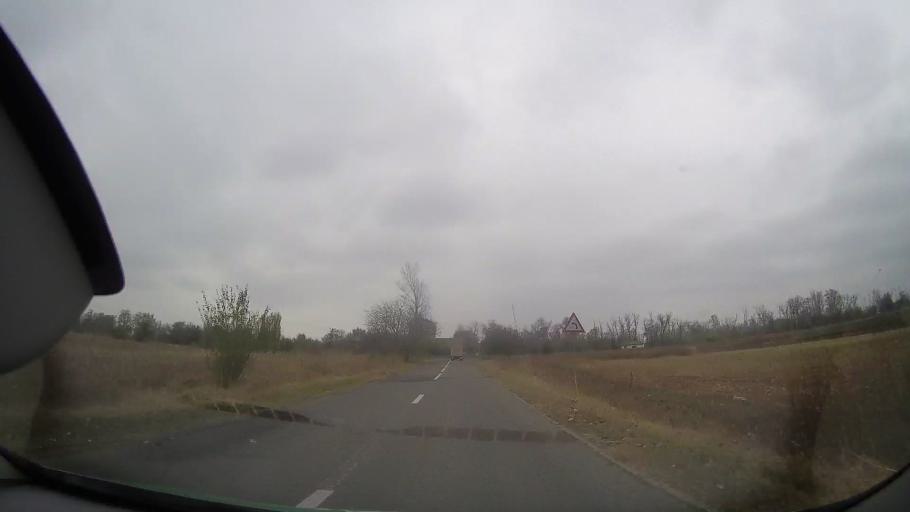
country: RO
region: Ialomita
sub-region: Comuna Garbovi
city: Garbovi
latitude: 44.7718
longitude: 26.7863
